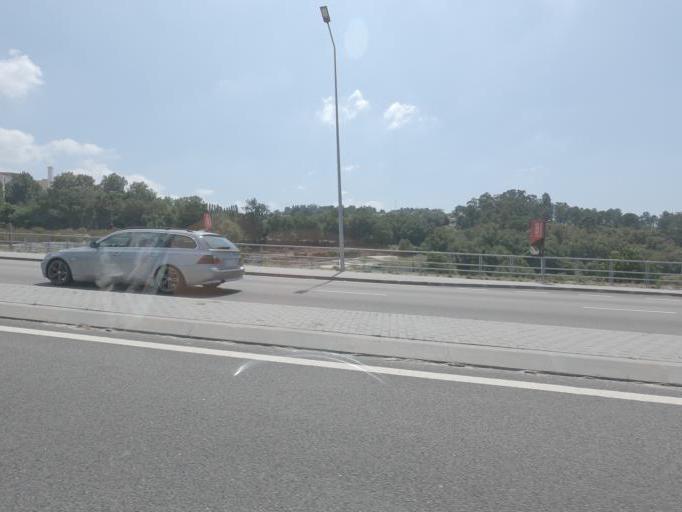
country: PT
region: Porto
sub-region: Paredes
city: Paredes
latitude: 41.2002
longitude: -8.3125
